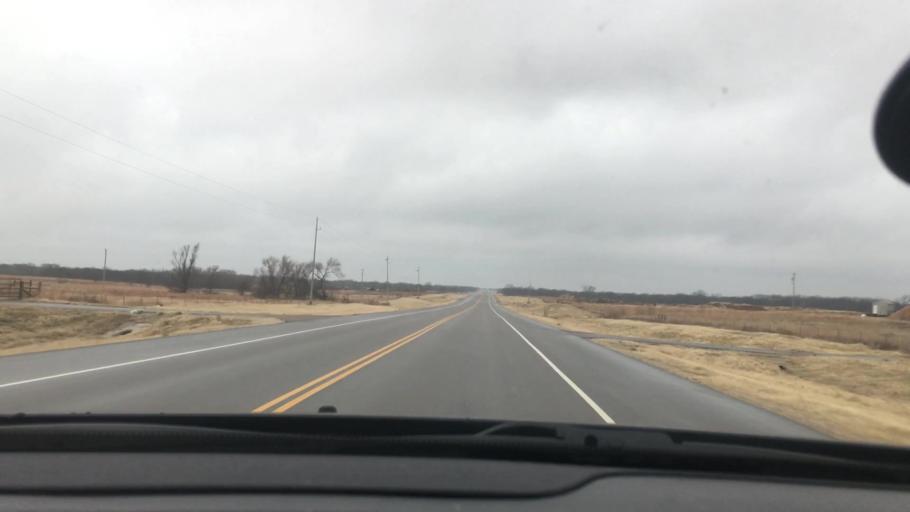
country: US
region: Oklahoma
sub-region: Johnston County
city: Tishomingo
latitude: 34.3418
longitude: -96.6422
